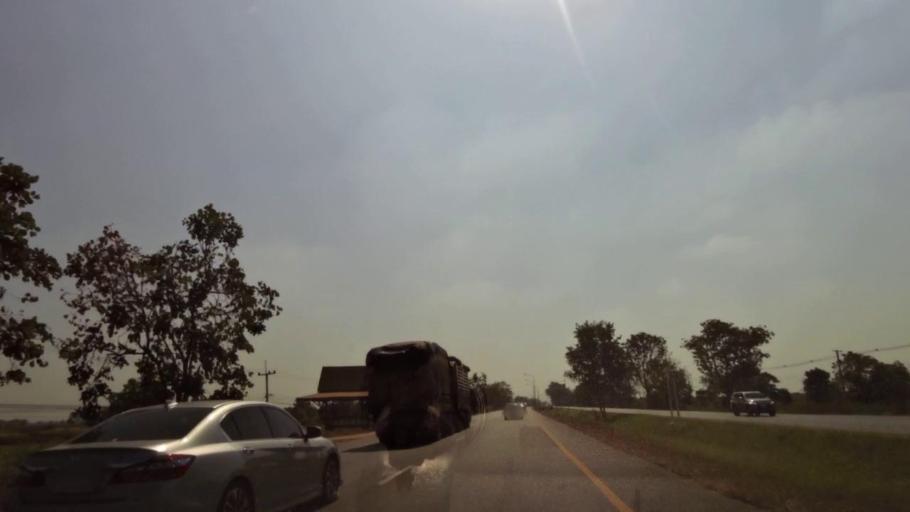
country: TH
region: Phichit
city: Wachira Barami
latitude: 16.4645
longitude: 100.1471
